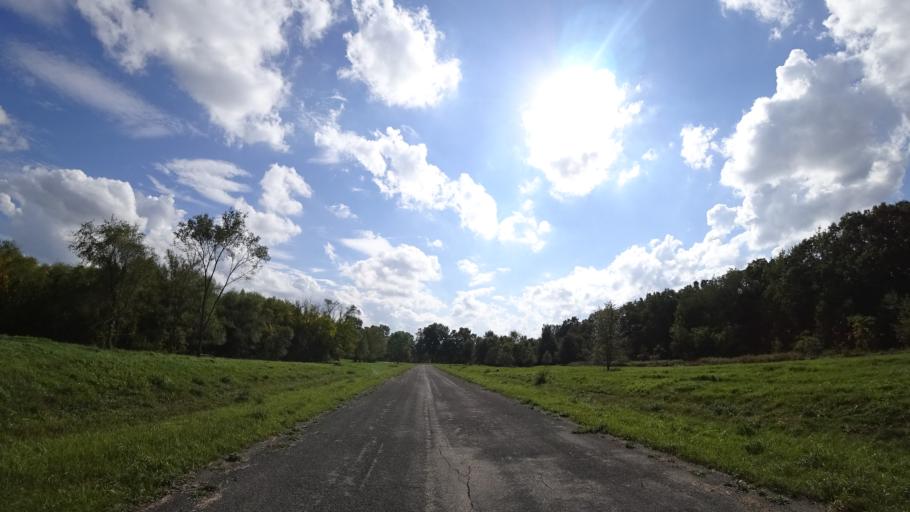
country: US
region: Michigan
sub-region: Saint Joseph County
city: Three Rivers
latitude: 41.9453
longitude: -85.6082
